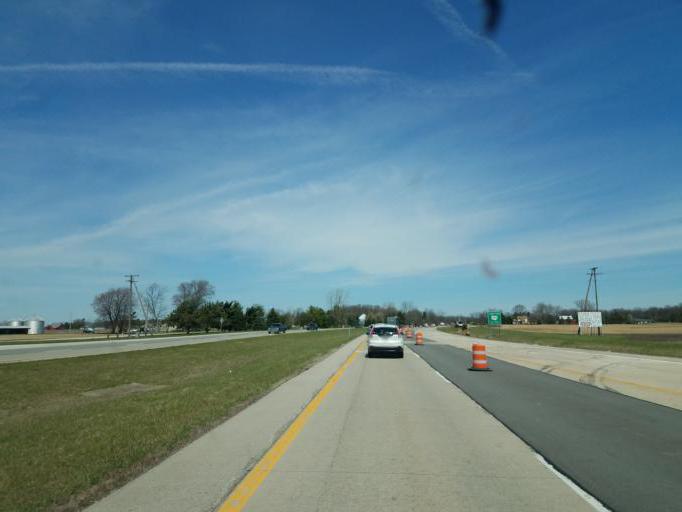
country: US
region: Ohio
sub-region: Marion County
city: Prospect
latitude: 40.4257
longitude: -83.0742
